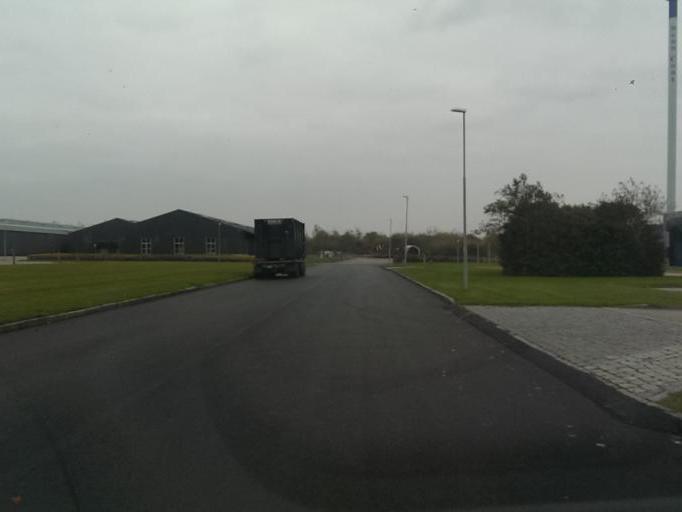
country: DK
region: South Denmark
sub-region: Esbjerg Kommune
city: Esbjerg
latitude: 55.5072
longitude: 8.4752
